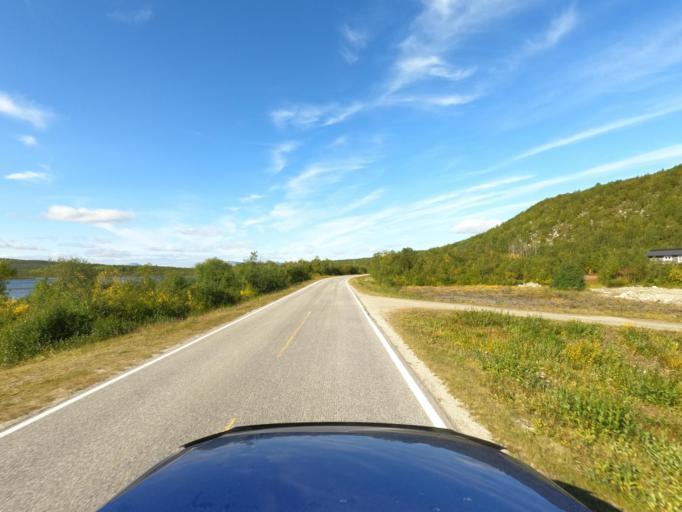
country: NO
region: Finnmark Fylke
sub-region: Porsanger
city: Lakselv
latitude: 69.7588
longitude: 25.2079
